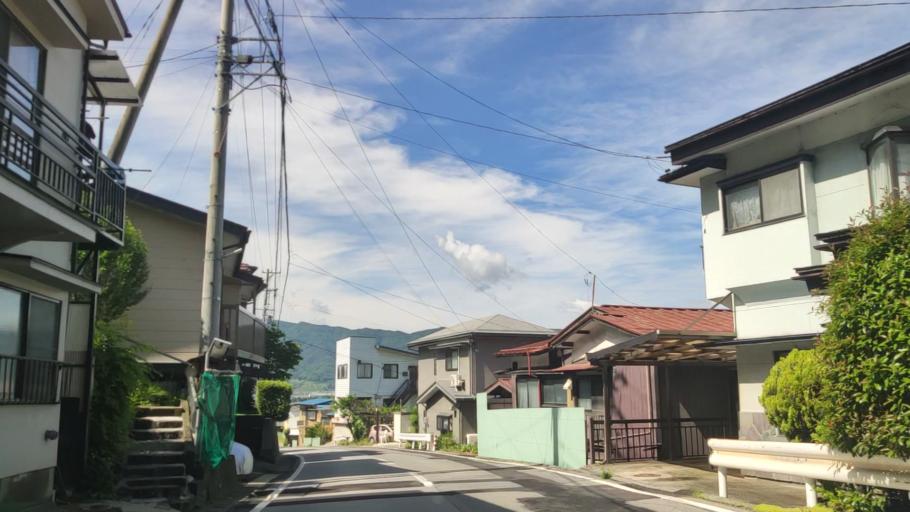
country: JP
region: Nagano
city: Suwa
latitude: 36.0418
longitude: 138.1263
